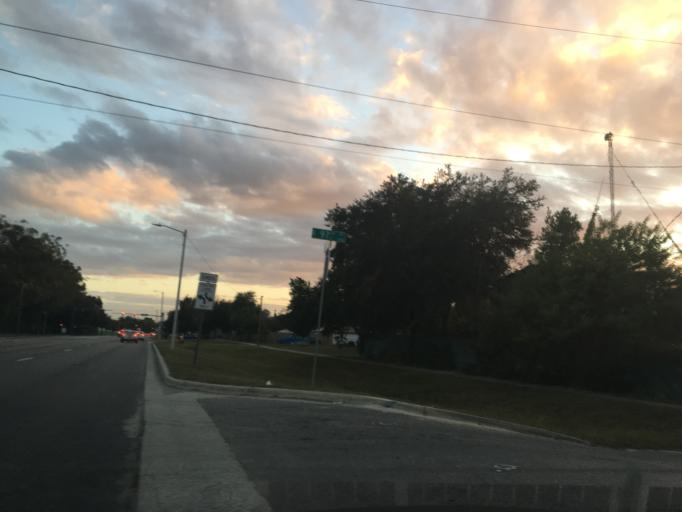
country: US
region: Florida
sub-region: Hillsborough County
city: University
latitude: 28.0377
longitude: -82.4263
